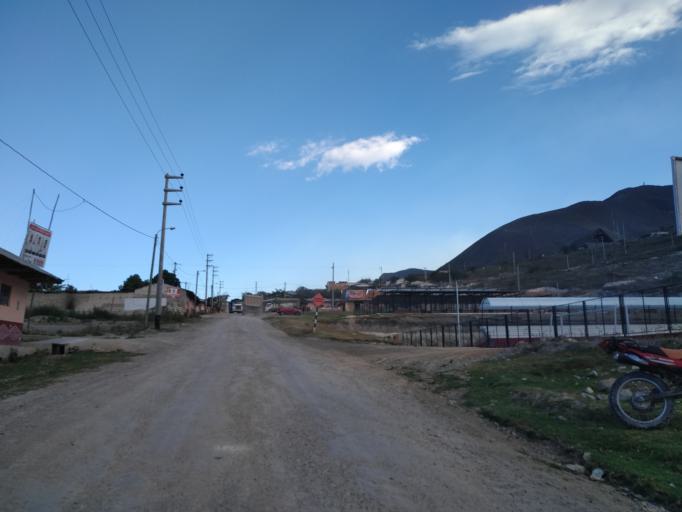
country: PE
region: Amazonas
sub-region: Provincia de Luya
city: Tingo
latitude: -6.3729
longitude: -77.9122
